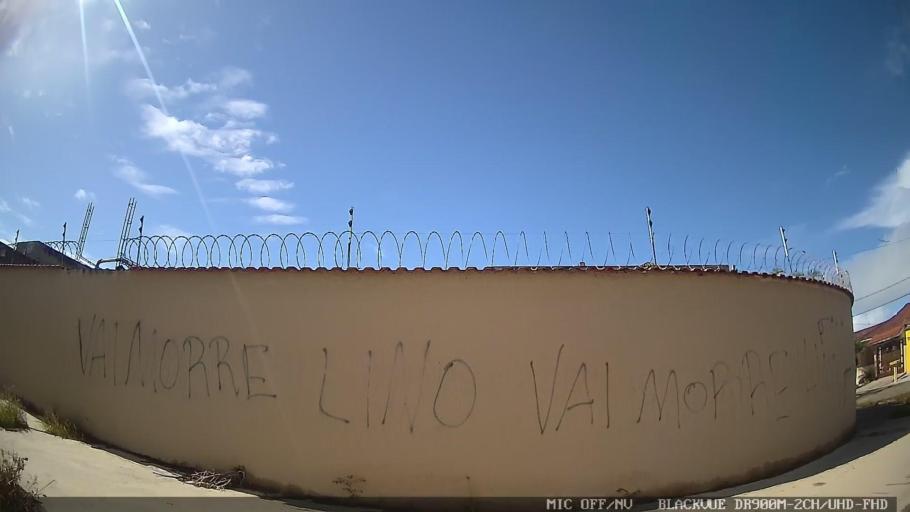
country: BR
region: Sao Paulo
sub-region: Itanhaem
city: Itanhaem
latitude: -24.2416
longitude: -46.8859
